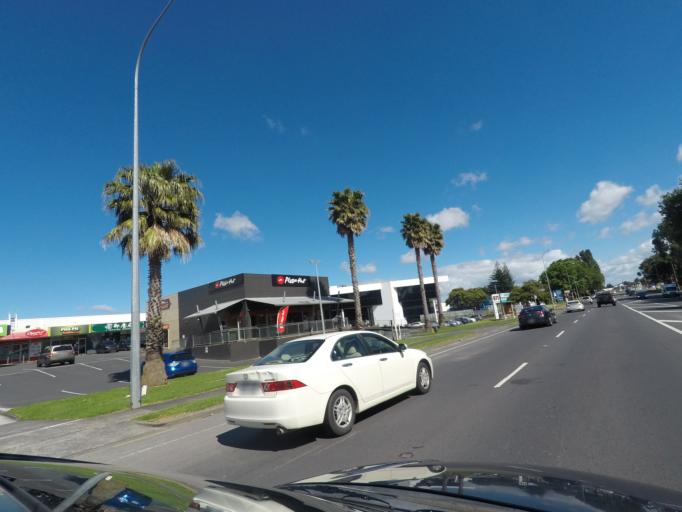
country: NZ
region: Auckland
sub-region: Auckland
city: Manukau City
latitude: -36.9863
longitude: 174.8808
